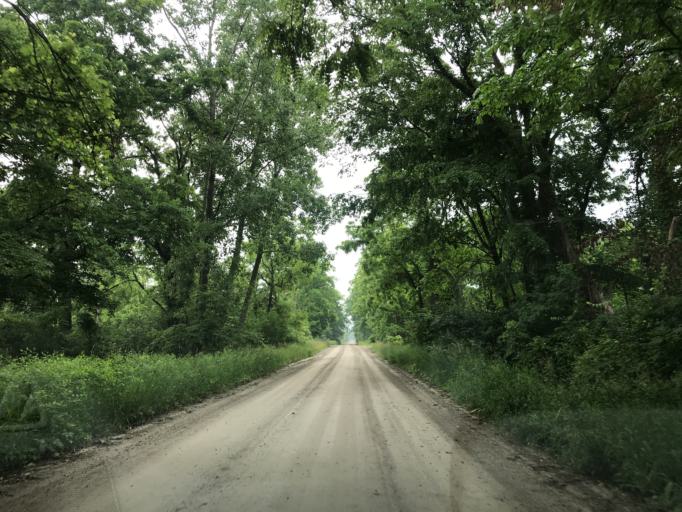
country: US
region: Michigan
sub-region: Washtenaw County
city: Ypsilanti
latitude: 42.2896
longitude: -83.6206
